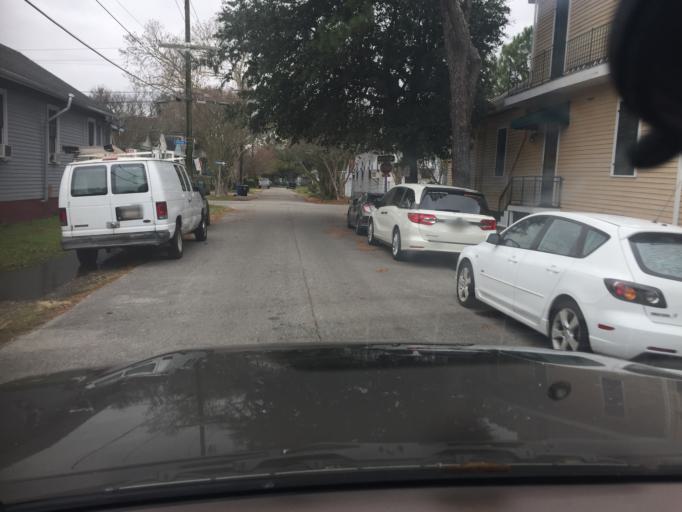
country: US
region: Louisiana
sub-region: Orleans Parish
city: New Orleans
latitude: 29.9816
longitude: -90.0762
